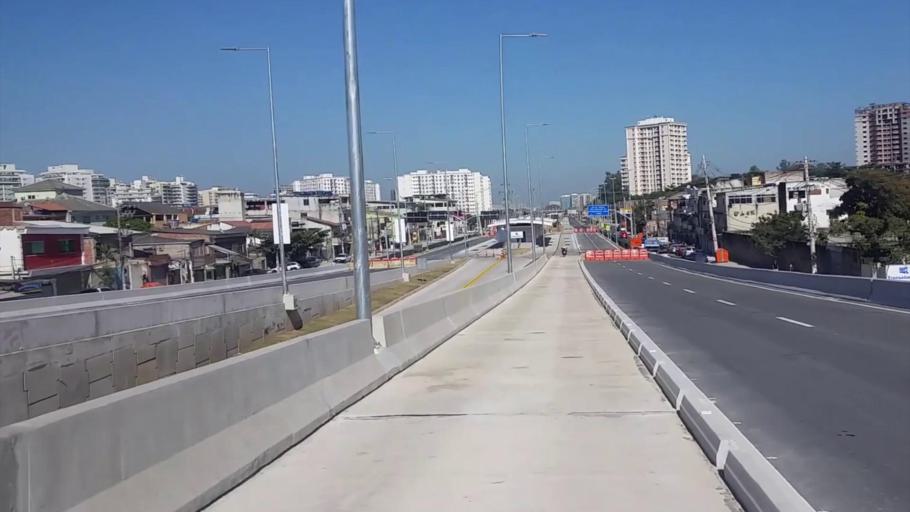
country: BR
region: Rio de Janeiro
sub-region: Nilopolis
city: Nilopolis
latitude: -22.9536
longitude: -43.3910
